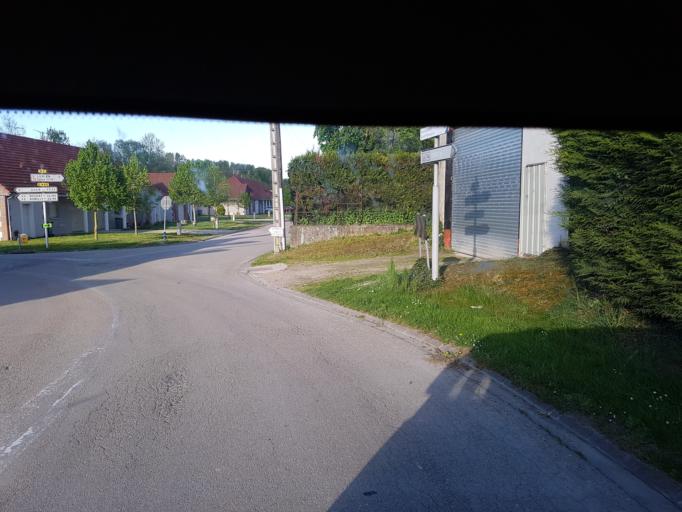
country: FR
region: Champagne-Ardenne
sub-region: Departement de l'Aube
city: Marigny-le-Chatel
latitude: 48.3482
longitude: 3.6352
